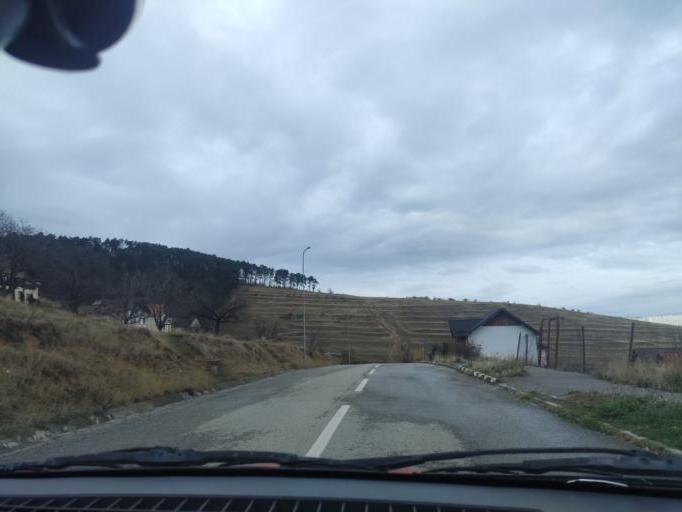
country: RO
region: Brasov
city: Codlea
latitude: 45.7073
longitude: 25.4426
